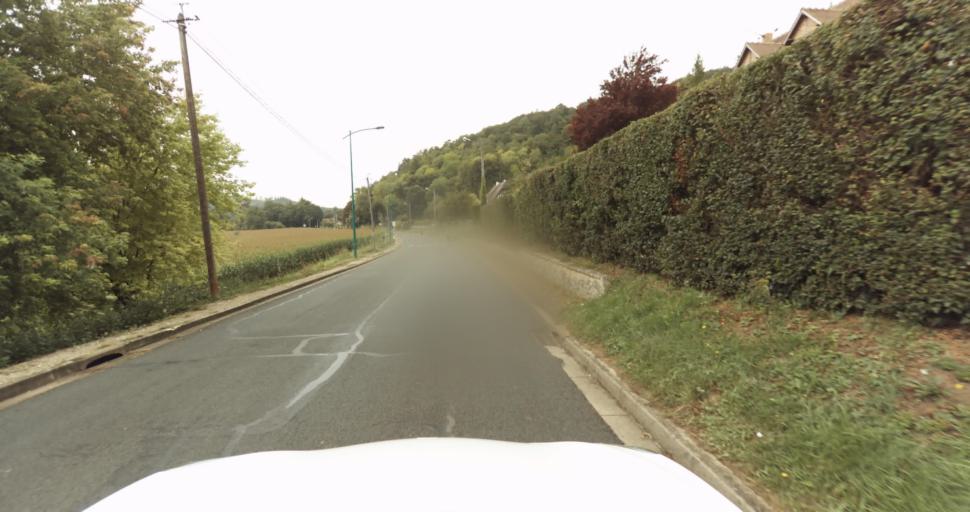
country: FR
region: Haute-Normandie
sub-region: Departement de l'Eure
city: Normanville
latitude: 49.0804
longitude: 1.1564
